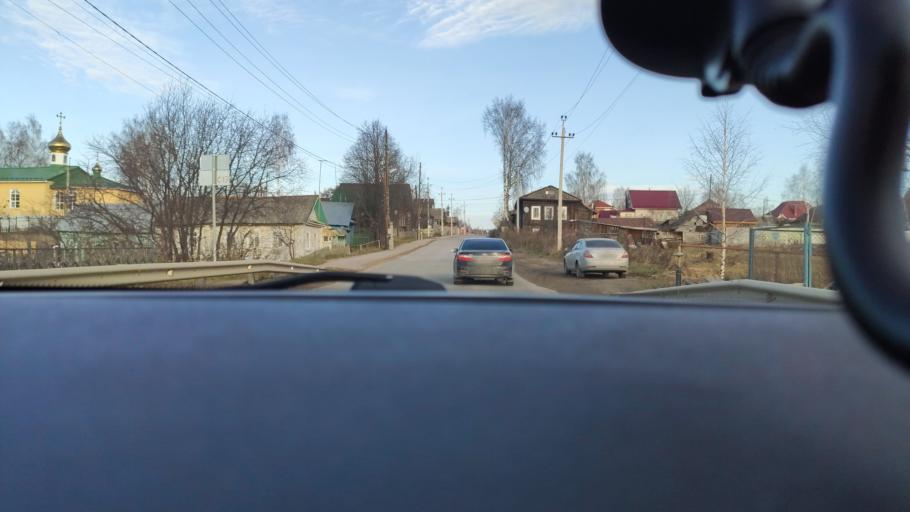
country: RU
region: Perm
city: Kondratovo
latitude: 58.0510
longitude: 56.0295
